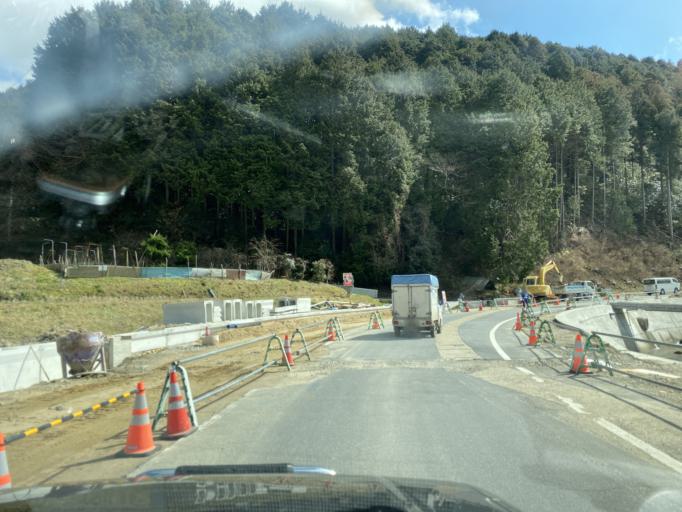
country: JP
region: Nara
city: Nara-shi
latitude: 34.7079
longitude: 135.9507
